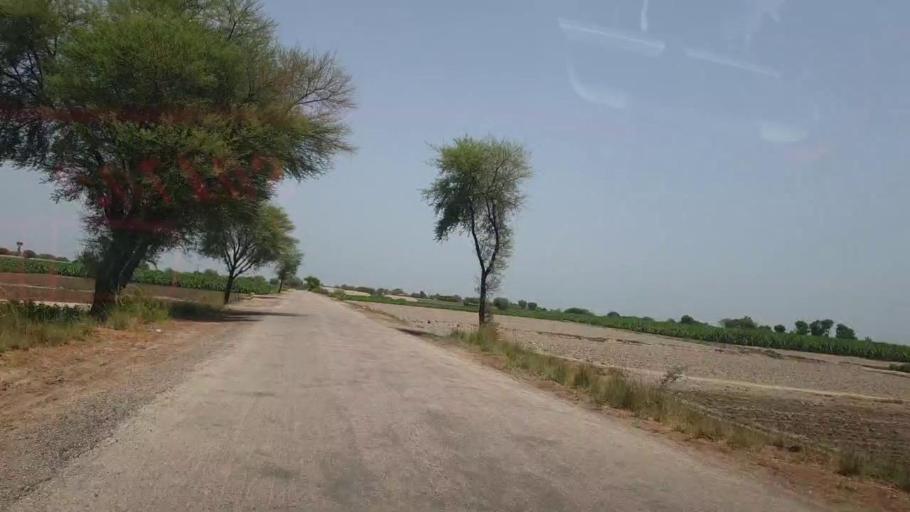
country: PK
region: Sindh
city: Daulatpur
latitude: 26.3882
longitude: 68.0540
